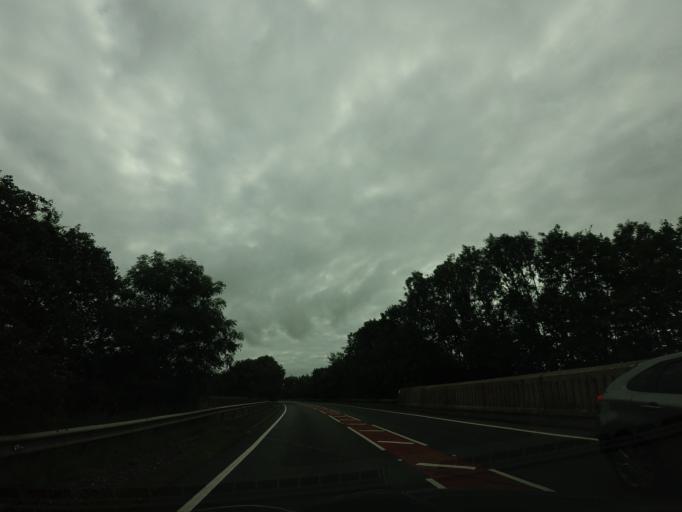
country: GB
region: Scotland
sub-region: Dumfries and Galloway
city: Gretna
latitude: 54.9925
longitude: -3.1146
